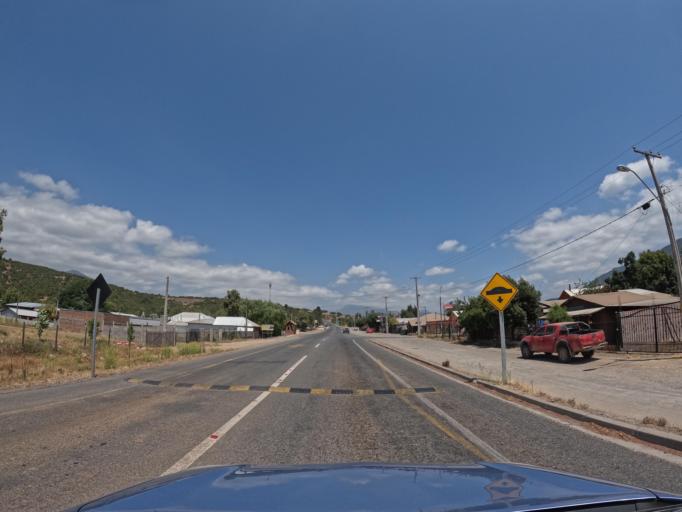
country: CL
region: Maule
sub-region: Provincia de Curico
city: Molina
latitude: -35.1773
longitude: -71.1213
